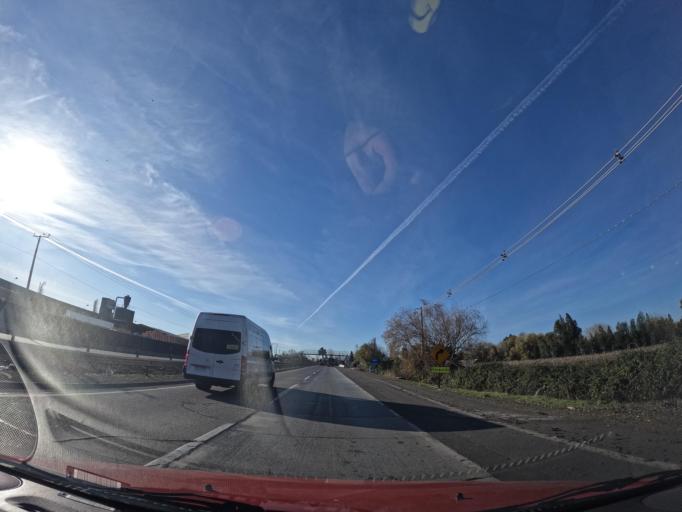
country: CL
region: Maule
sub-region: Provincia de Linares
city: San Javier
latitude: -35.5791
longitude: -71.7046
